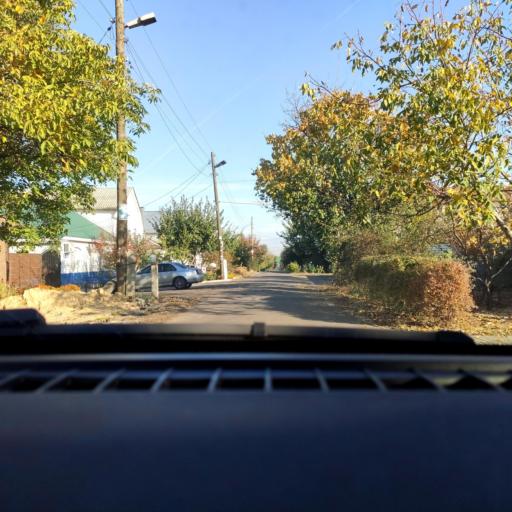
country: RU
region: Voronezj
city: Voronezh
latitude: 51.6641
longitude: 39.2634
